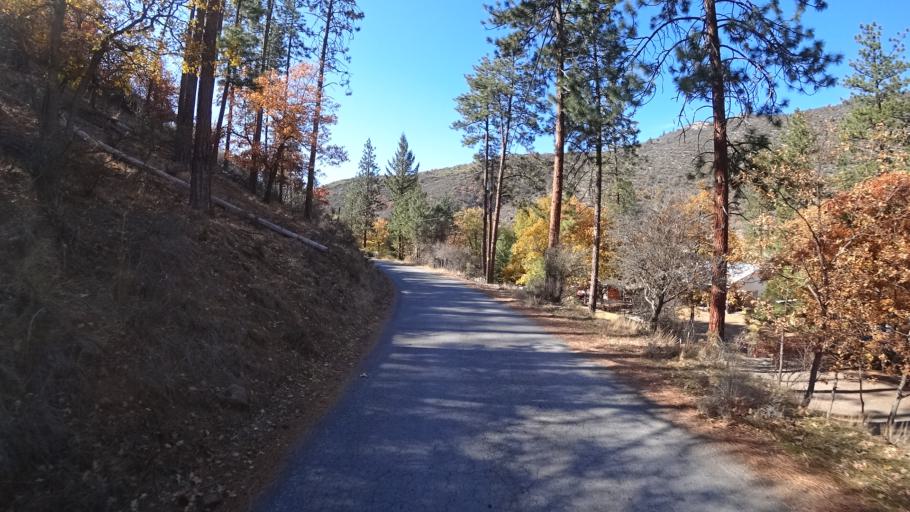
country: US
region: California
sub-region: Siskiyou County
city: Yreka
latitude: 41.8338
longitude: -122.6369
